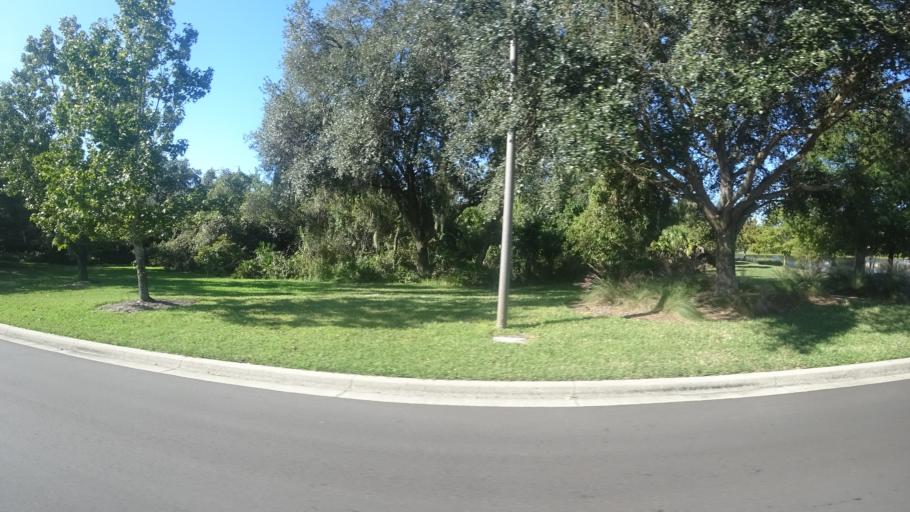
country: US
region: Florida
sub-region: Sarasota County
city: The Meadows
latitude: 27.4035
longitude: -82.4137
